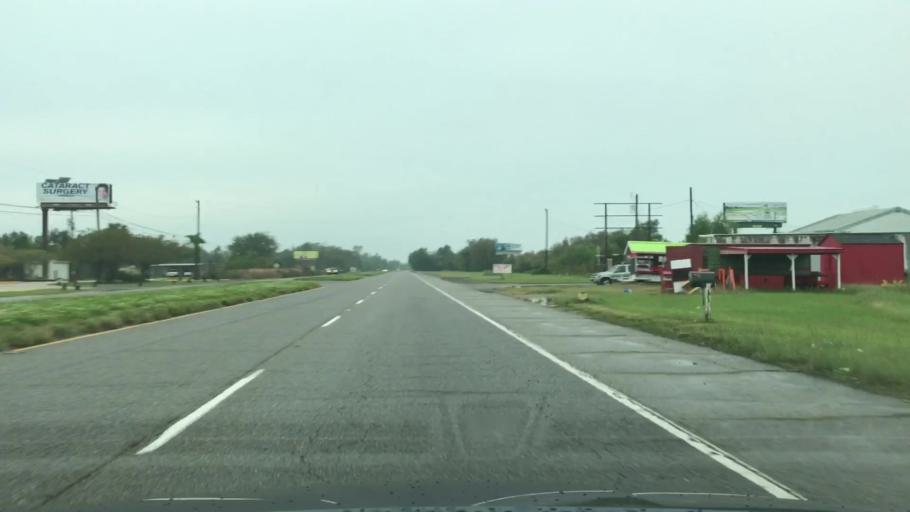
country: US
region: Louisiana
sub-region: Saint Charles Parish
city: Des Allemands
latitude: 29.8041
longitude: -90.4995
